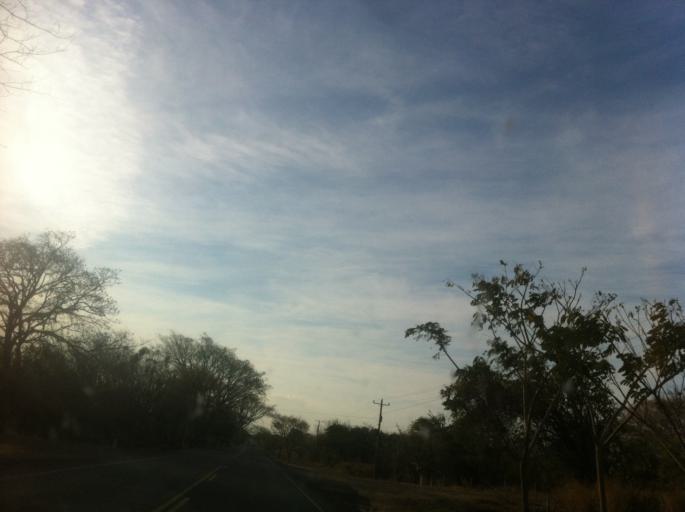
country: NI
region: Rivas
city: Rivas
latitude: 11.3759
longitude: -85.7604
